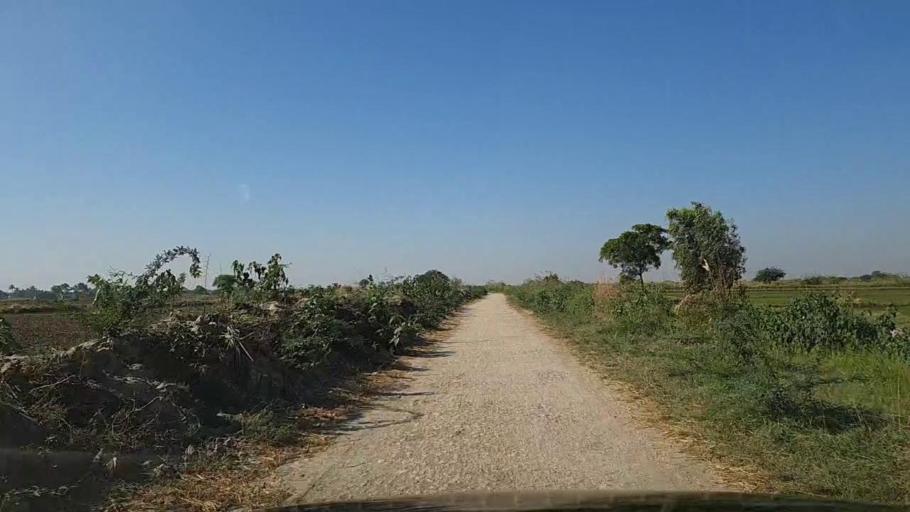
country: PK
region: Sindh
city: Thatta
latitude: 24.7174
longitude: 67.9230
